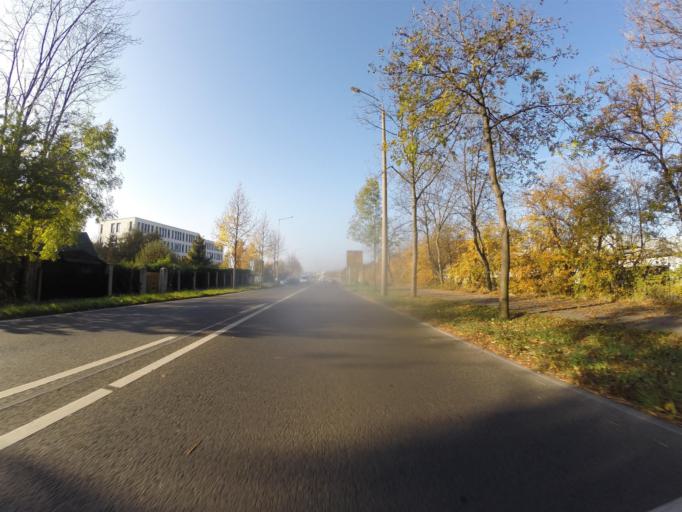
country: DE
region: Saxony
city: Leipzig
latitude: 51.3421
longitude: 12.3061
